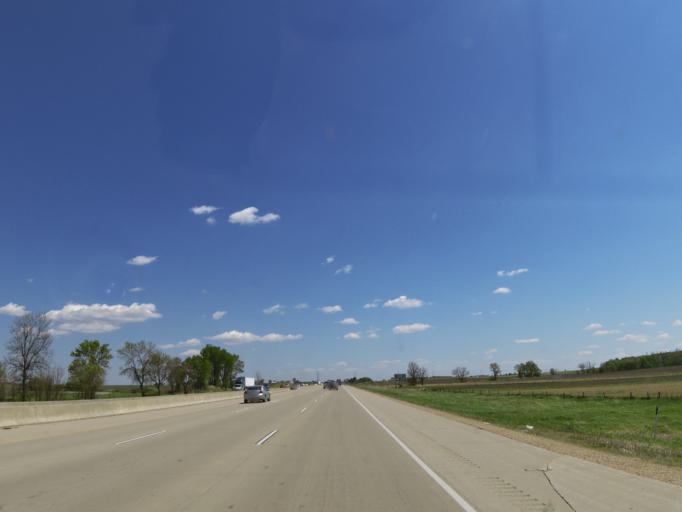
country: US
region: Wisconsin
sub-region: Dane County
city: De Forest
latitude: 43.2954
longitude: -89.4192
